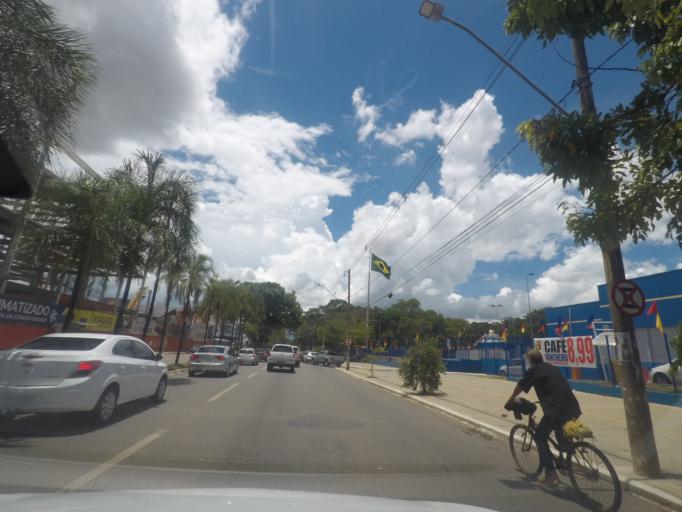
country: BR
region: Goias
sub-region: Goiania
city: Goiania
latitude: -16.6626
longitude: -49.2554
